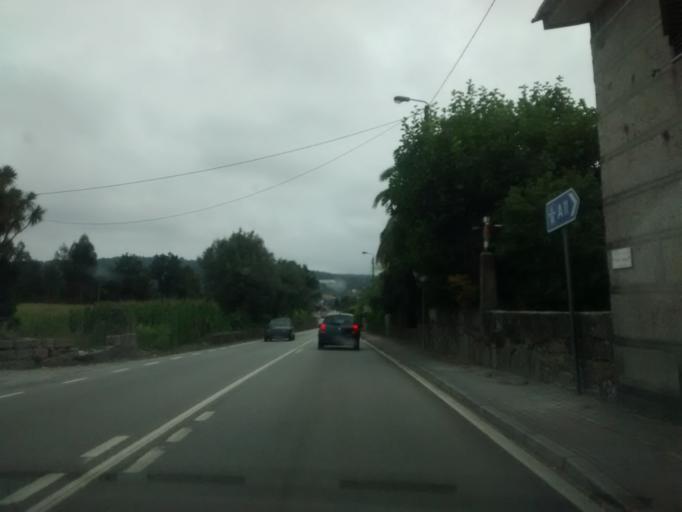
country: PT
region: Braga
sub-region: Braga
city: Oliveira
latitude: 41.4802
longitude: -8.4814
